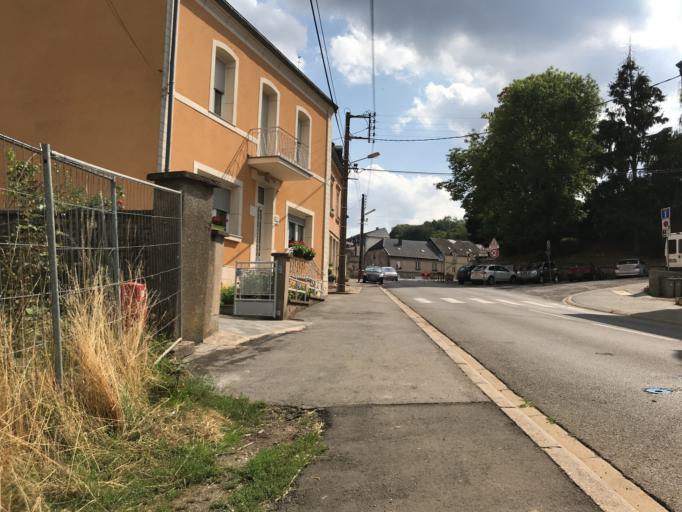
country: LU
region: Luxembourg
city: Belvaux
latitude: 49.4938
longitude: 5.9193
